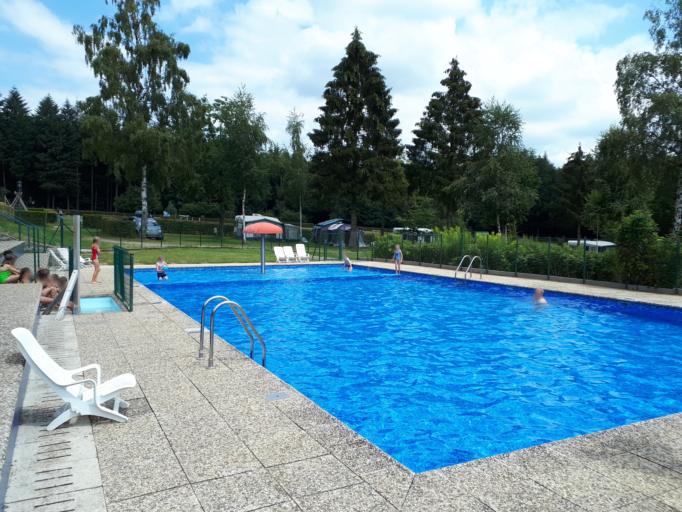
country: LU
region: Diekirch
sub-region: Canton de Diekirch
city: Medernach
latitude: 49.8001
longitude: 6.1984
